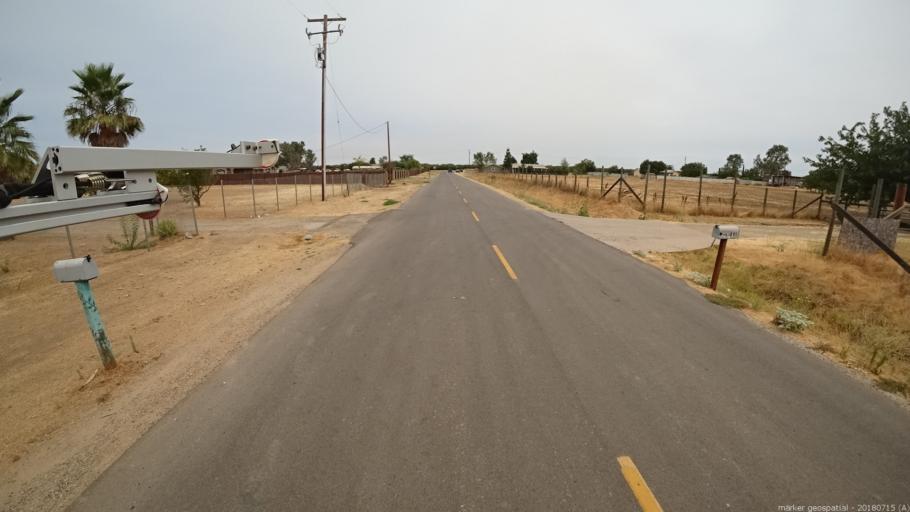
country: US
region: California
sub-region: Madera County
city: Madera Acres
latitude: 37.0236
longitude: -120.0866
